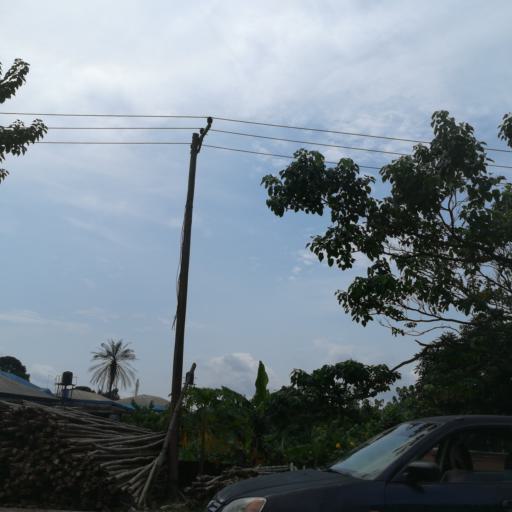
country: NG
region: Rivers
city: Port Harcourt
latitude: 4.8620
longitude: 7.0207
